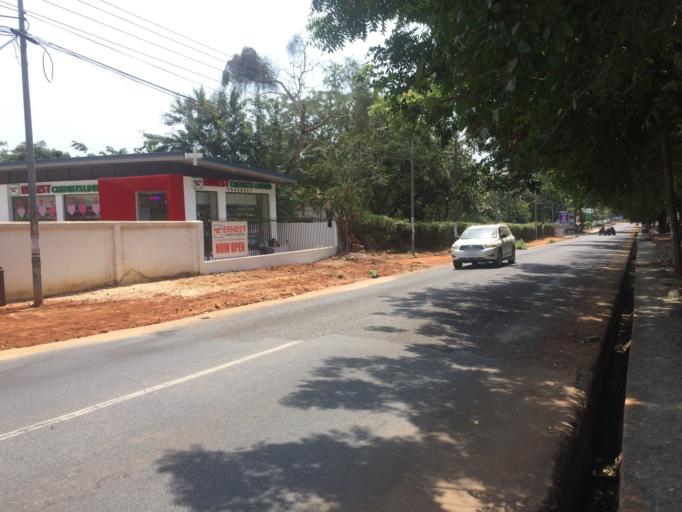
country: GH
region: Greater Accra
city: Accra
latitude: 5.5663
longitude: -0.1900
